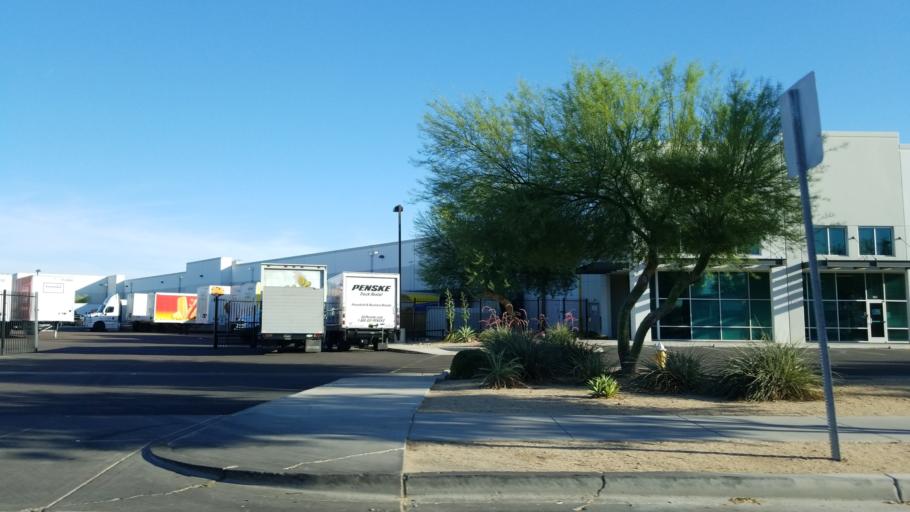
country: US
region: Arizona
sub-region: Maricopa County
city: Phoenix
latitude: 33.4512
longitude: -112.0070
